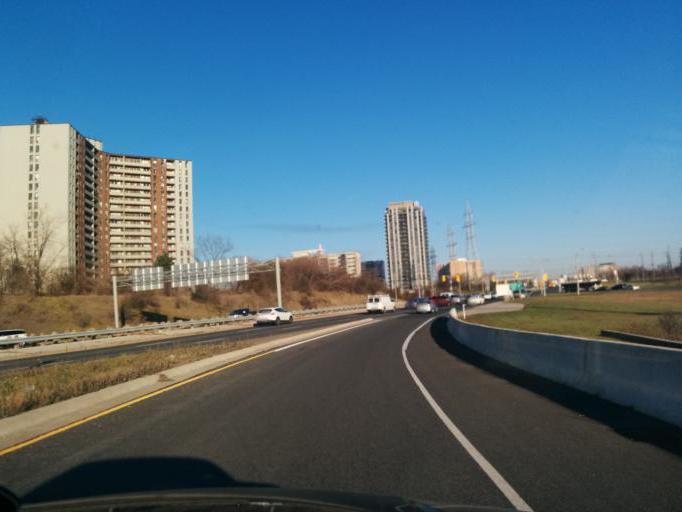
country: CA
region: Ontario
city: Etobicoke
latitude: 43.6735
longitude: -79.5699
